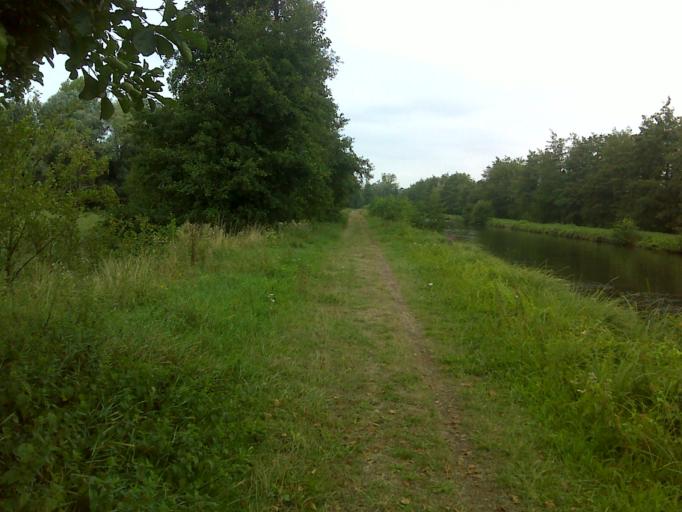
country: FR
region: Nord-Pas-de-Calais
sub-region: Departement du Nord
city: Landrecies
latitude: 50.1074
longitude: 3.6443
